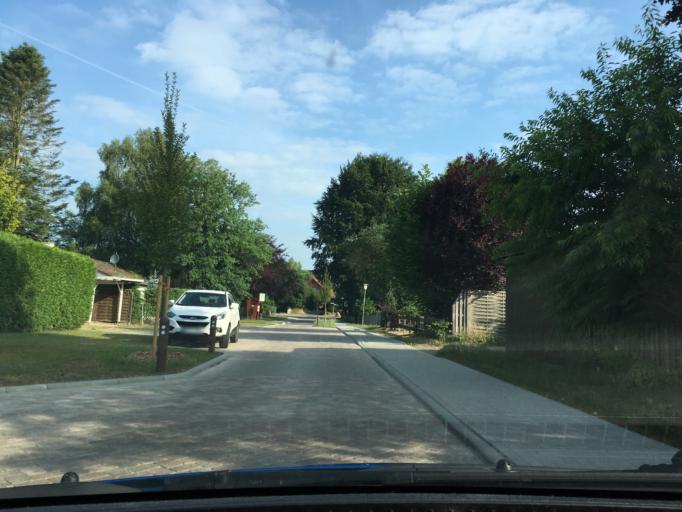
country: DE
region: Lower Saxony
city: Kakenstorf
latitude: 53.3109
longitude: 9.7741
